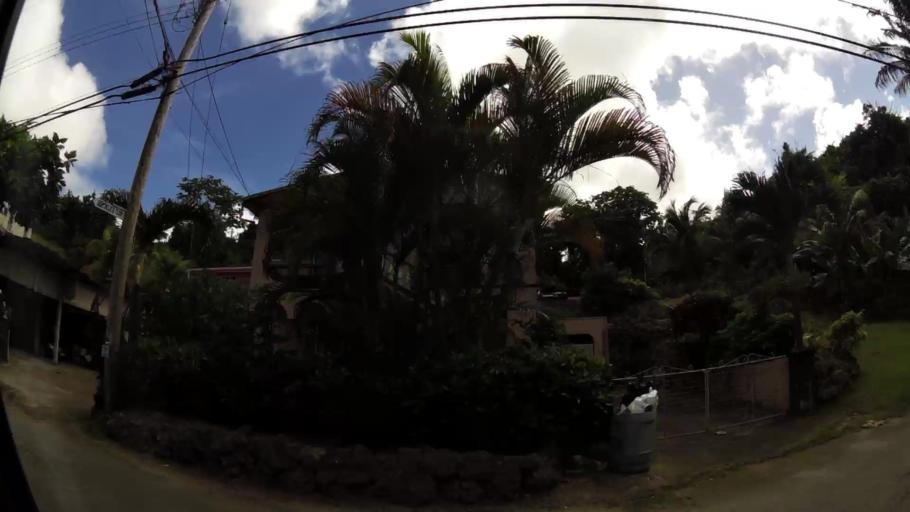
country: BB
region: Saint James
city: Holetown
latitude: 13.2079
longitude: -59.6055
